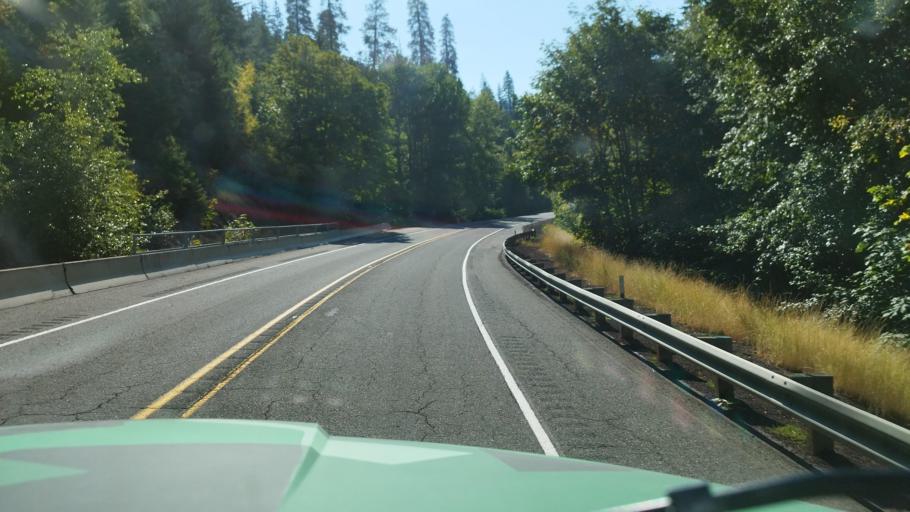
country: US
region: Oregon
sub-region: Hood River County
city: Odell
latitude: 45.5027
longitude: -121.5622
